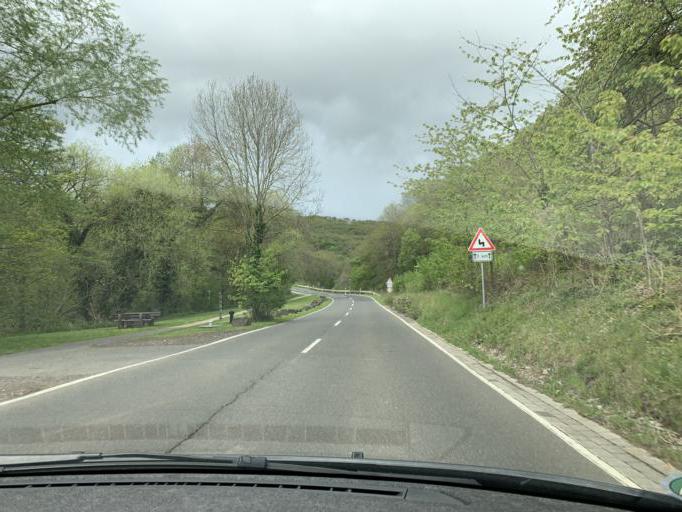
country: DE
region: North Rhine-Westphalia
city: Heimbach
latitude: 50.6375
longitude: 6.4723
